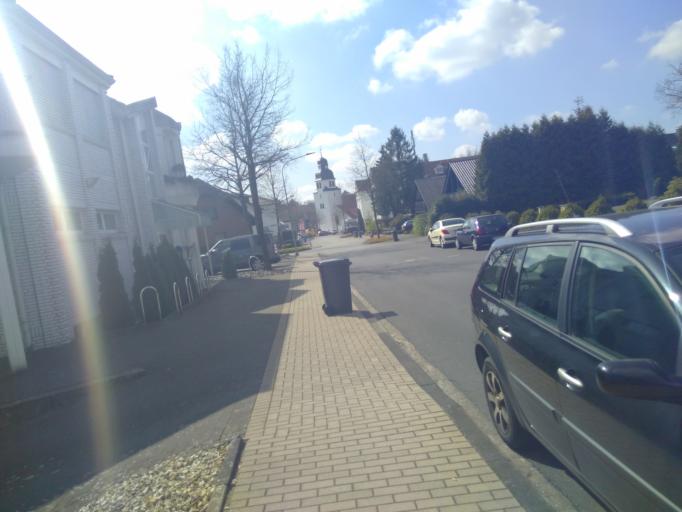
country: DE
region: North Rhine-Westphalia
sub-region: Regierungsbezirk Detmold
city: Oerlinghausen
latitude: 51.9143
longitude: 8.6583
